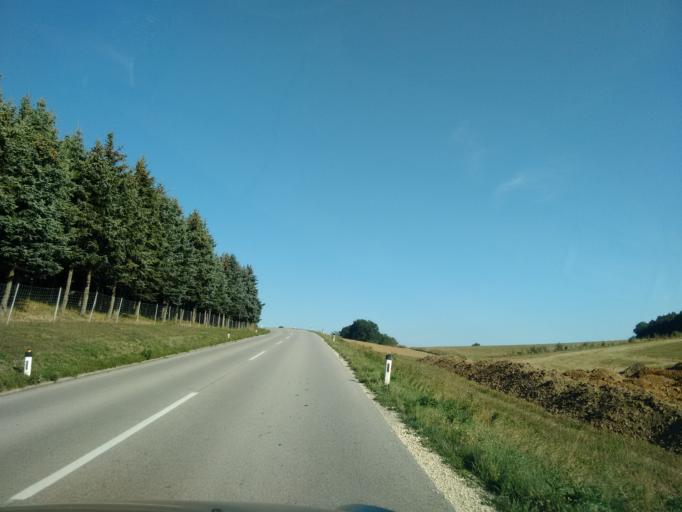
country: AT
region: Upper Austria
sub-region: Wels-Land
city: Marchtrenk
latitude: 48.1477
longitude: 14.1845
